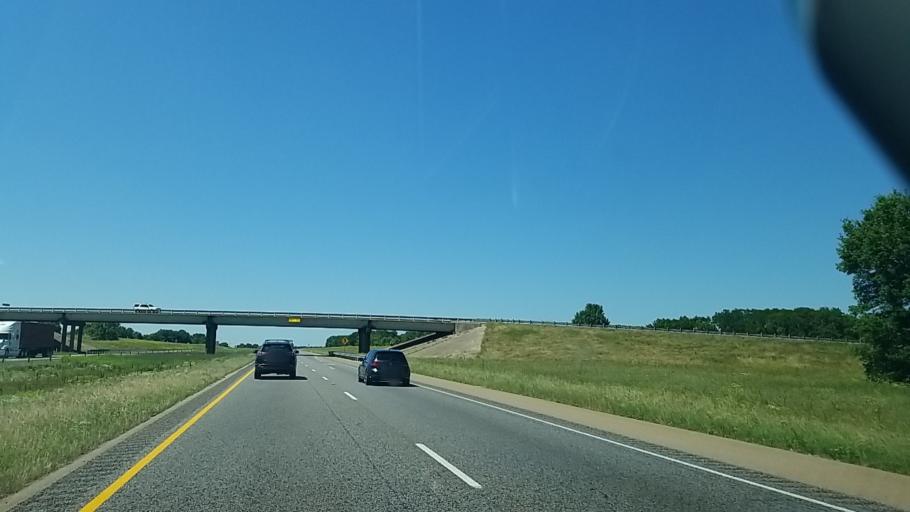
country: US
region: Texas
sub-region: Freestone County
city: Fairfield
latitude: 31.5963
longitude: -96.1535
